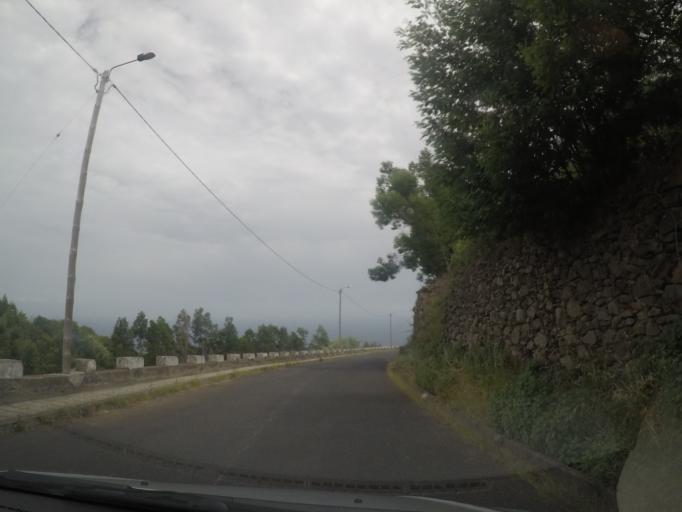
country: PT
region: Madeira
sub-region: Santa Cruz
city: Santa Cruz
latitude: 32.6789
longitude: -16.8100
